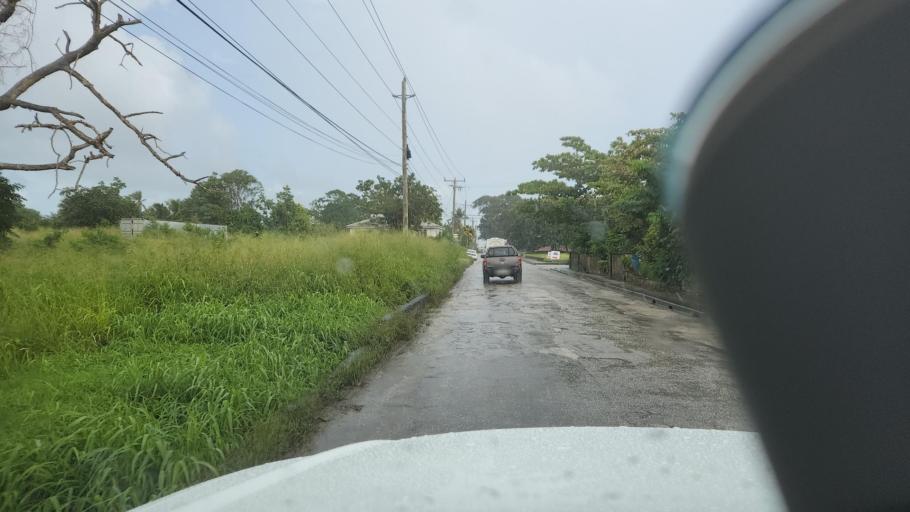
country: BB
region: Saint Michael
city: Bridgetown
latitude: 13.1169
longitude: -59.5755
